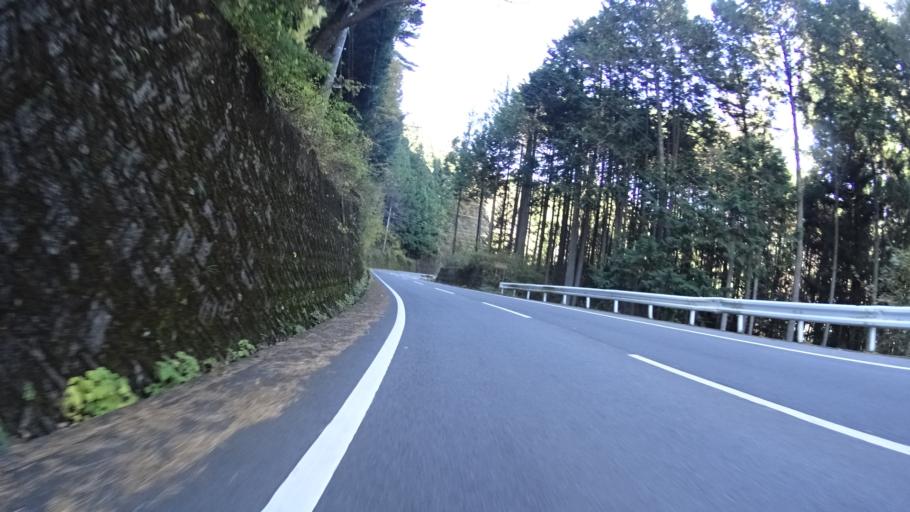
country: JP
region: Yamanashi
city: Otsuki
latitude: 35.7489
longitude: 138.9556
